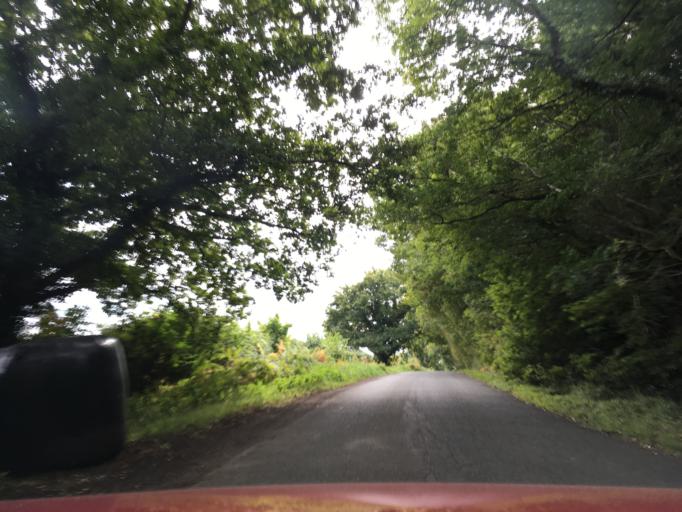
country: GB
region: England
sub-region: South Gloucestershire
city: Charfield
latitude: 51.6525
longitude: -2.4221
